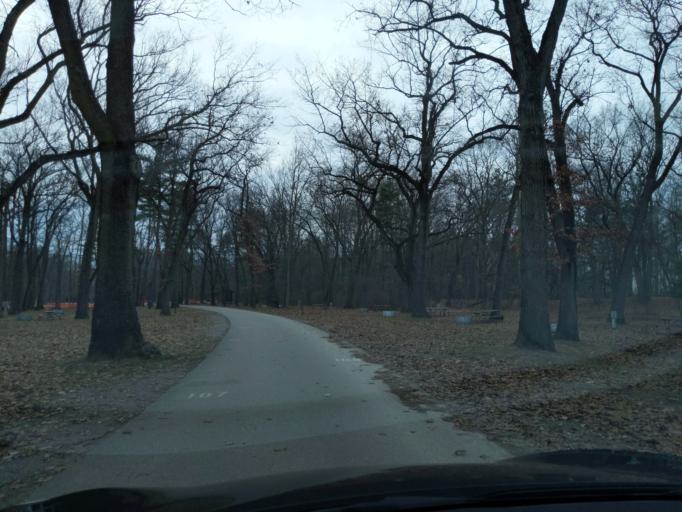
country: US
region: Michigan
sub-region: Bay County
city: Bay City
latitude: 43.6648
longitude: -83.9020
